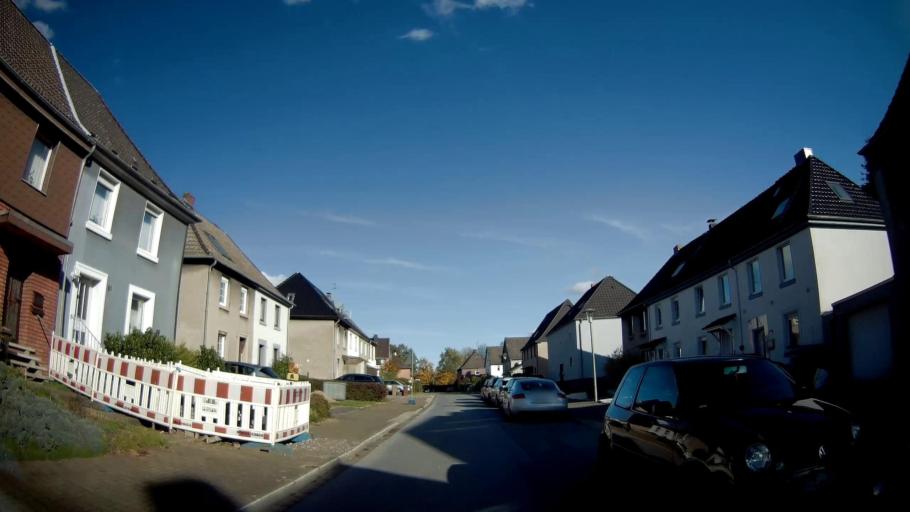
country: DE
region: North Rhine-Westphalia
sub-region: Regierungsbezirk Munster
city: Gladbeck
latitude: 51.5630
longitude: 7.0063
